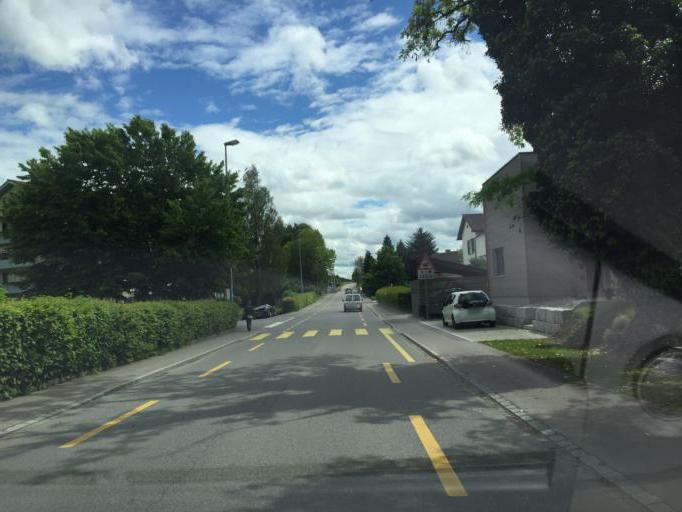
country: CH
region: Thurgau
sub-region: Frauenfeld District
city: Diessenhofen
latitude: 47.6848
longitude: 8.7564
